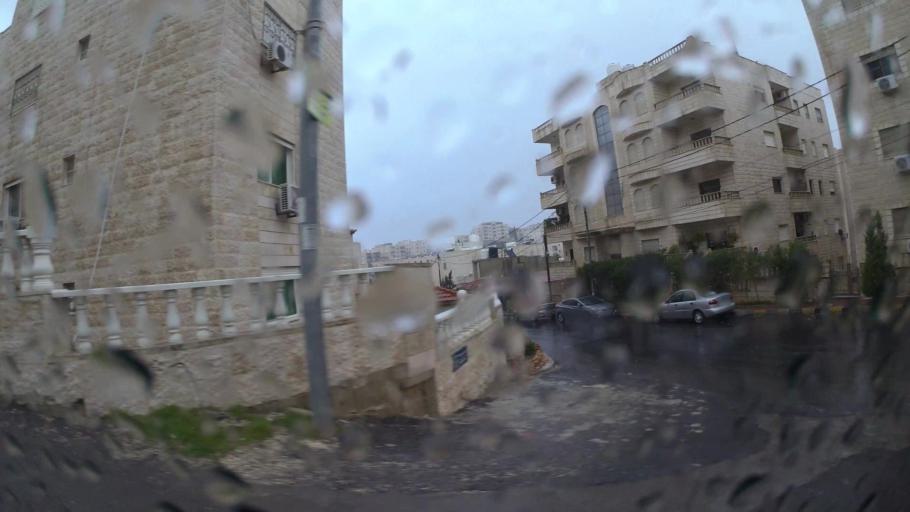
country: JO
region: Amman
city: Amman
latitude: 32.0048
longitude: 35.9313
